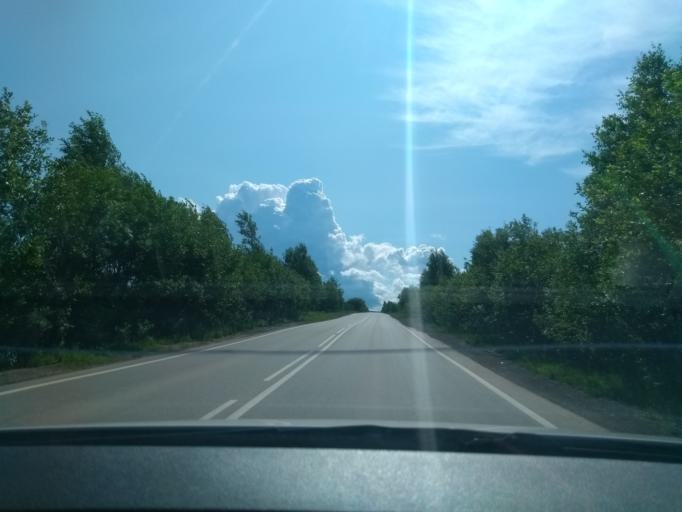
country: RU
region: Perm
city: Bershet'
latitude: 57.8159
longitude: 56.4459
